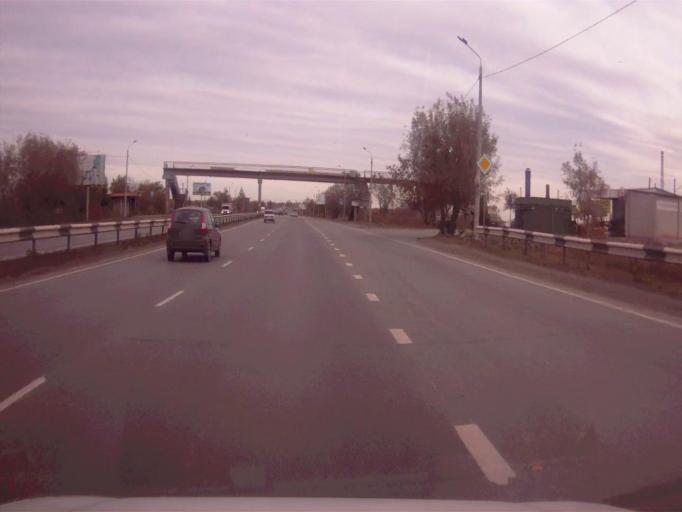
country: RU
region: Chelyabinsk
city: Novosineglazovskiy
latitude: 55.0427
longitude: 61.4268
